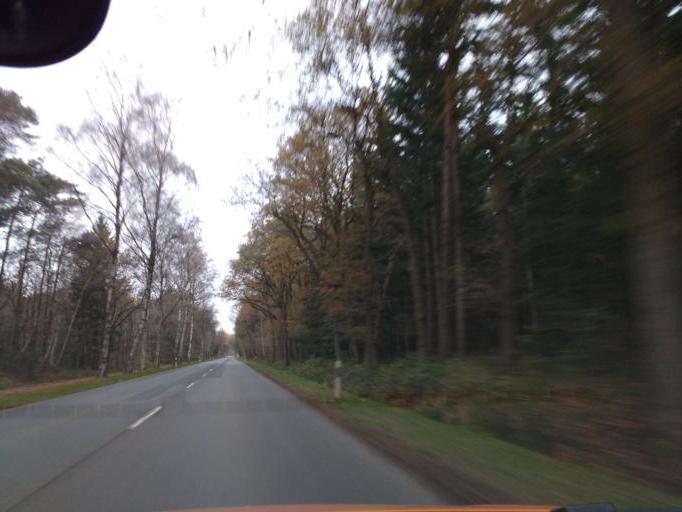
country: DE
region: Lower Saxony
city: Hatten
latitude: 53.0739
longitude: 8.4149
